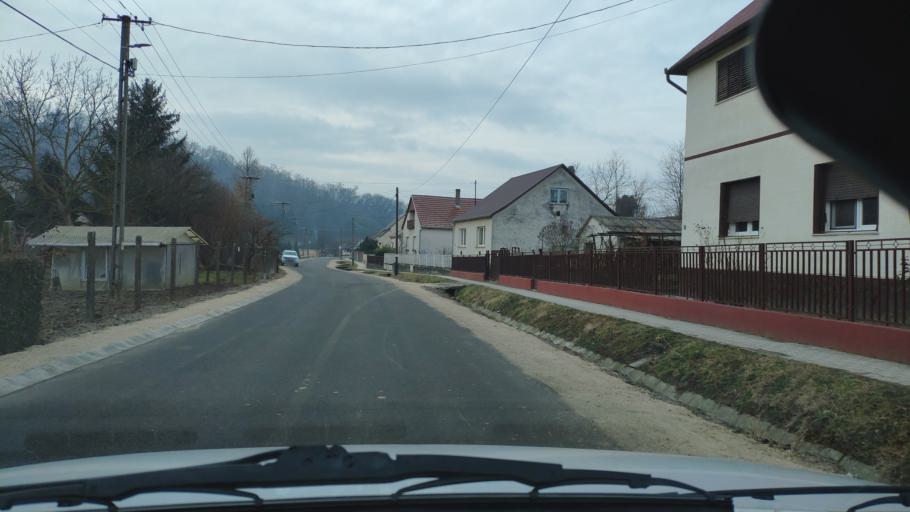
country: HU
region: Zala
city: Nagykanizsa
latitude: 46.5390
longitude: 16.9894
